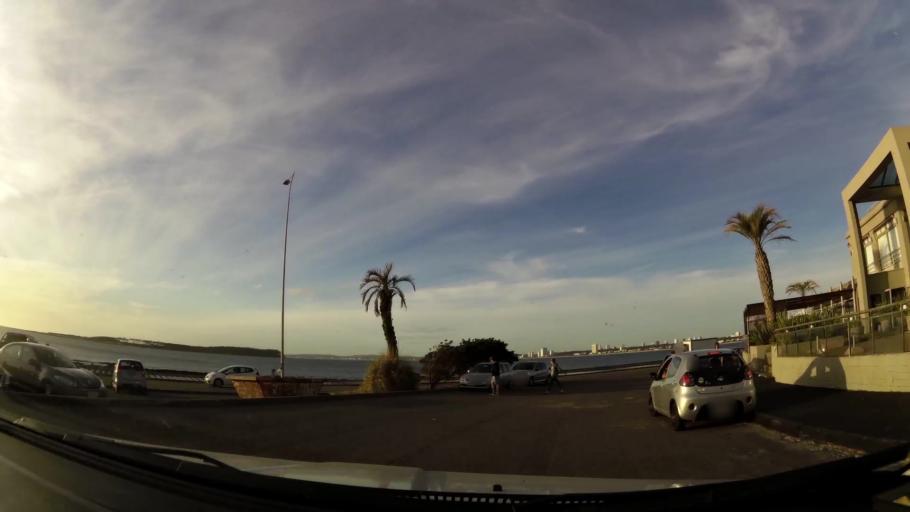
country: UY
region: Maldonado
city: Punta del Este
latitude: -34.9650
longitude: -54.9536
